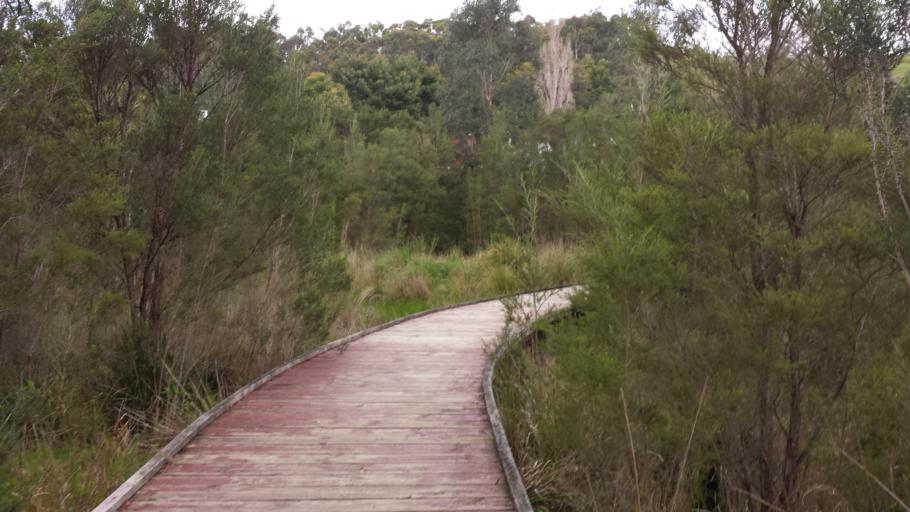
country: AU
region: Victoria
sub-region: Yarra Ranges
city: Belgrave South
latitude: -37.9242
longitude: 145.3329
